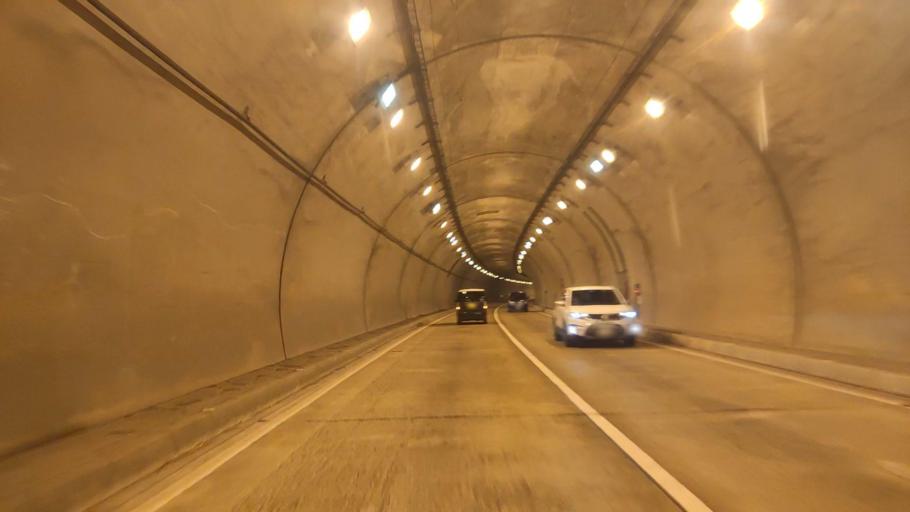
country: JP
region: Fukui
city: Takefu
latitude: 35.8204
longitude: 136.1023
